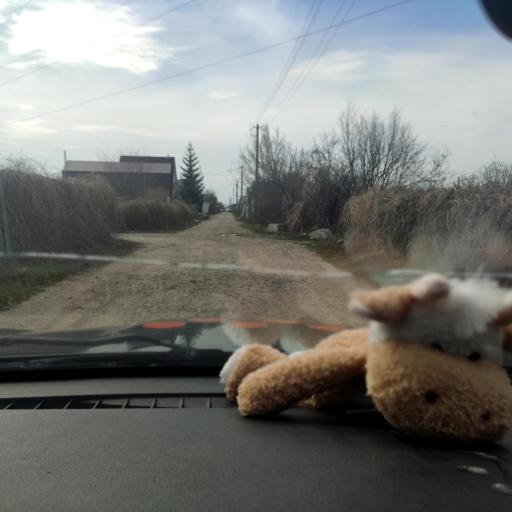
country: RU
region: Samara
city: Tol'yatti
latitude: 53.5941
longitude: 49.2380
